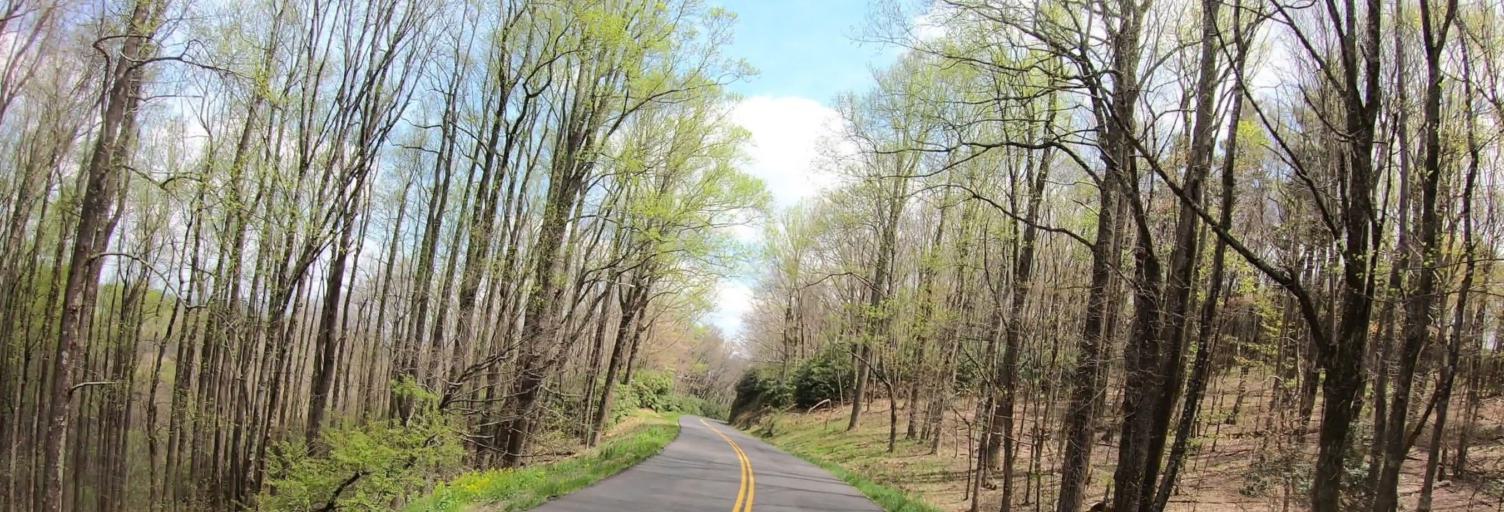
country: US
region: Virginia
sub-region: Carroll County
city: Cana
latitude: 36.6683
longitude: -80.6794
